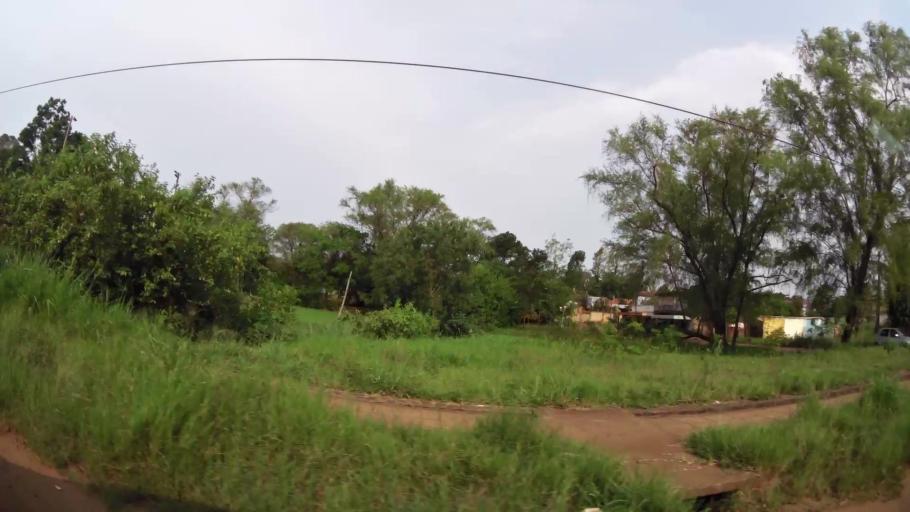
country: PY
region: Alto Parana
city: Ciudad del Este
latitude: -25.4953
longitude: -54.6587
